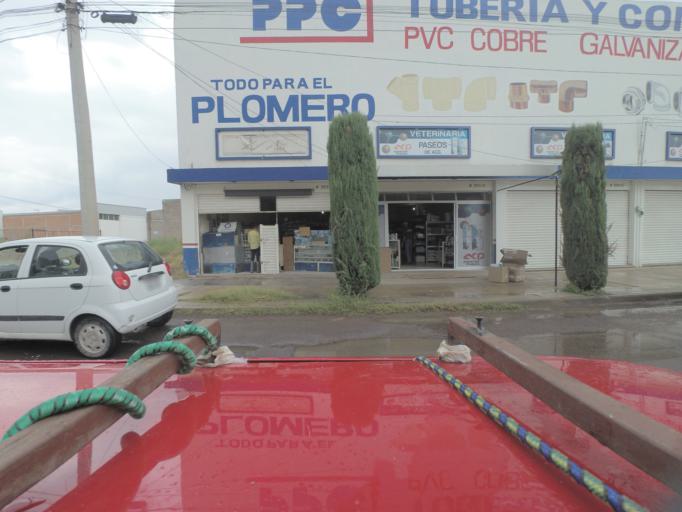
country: MX
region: Aguascalientes
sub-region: Jesus Maria
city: Arboledas Paso Blanco [Fraccionamiento]
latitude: 21.9672
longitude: -102.2921
